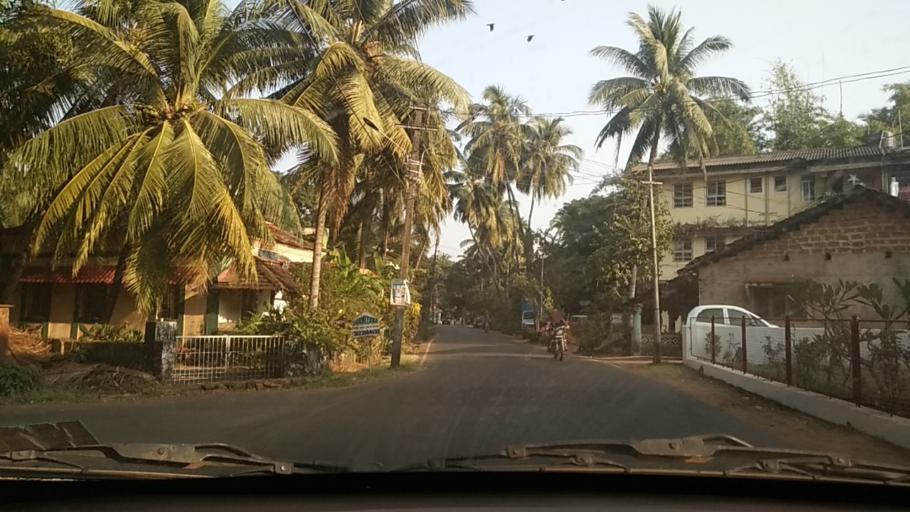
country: IN
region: Goa
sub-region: North Goa
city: Bambolim
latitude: 15.4871
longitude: 73.8509
